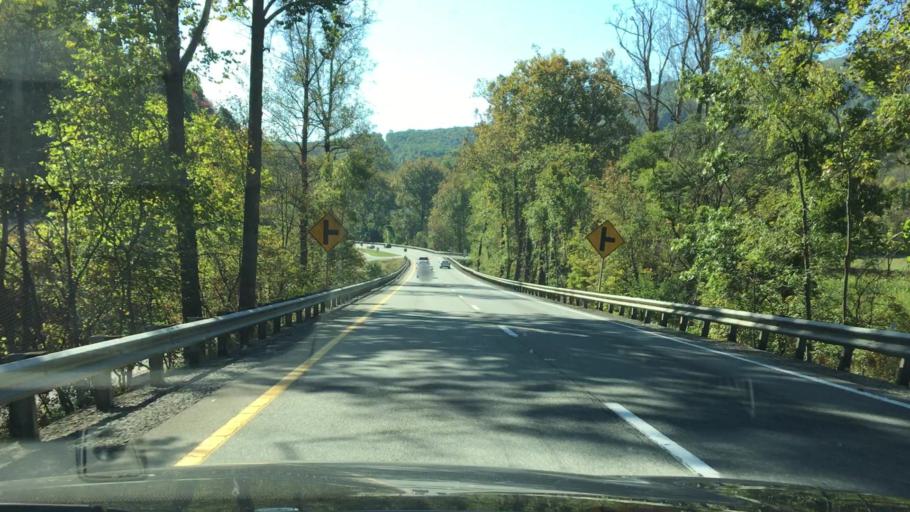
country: US
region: Virginia
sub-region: Roanoke County
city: Narrows
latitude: 37.1363
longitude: -79.9730
